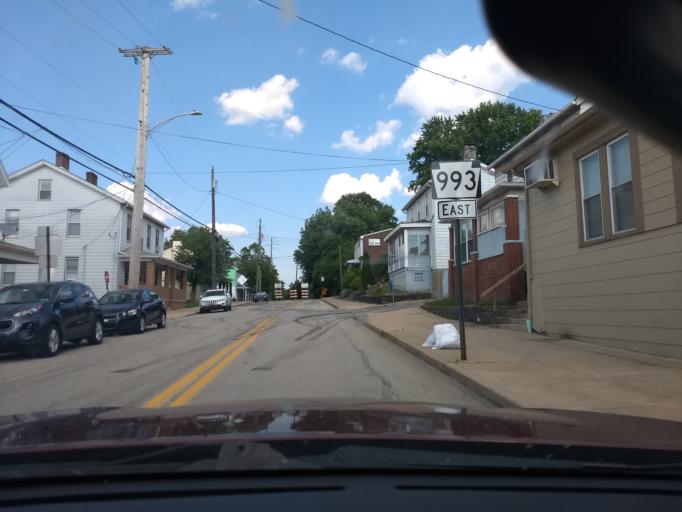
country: US
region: Pennsylvania
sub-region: Westmoreland County
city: Irwin
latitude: 40.3325
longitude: -79.7091
